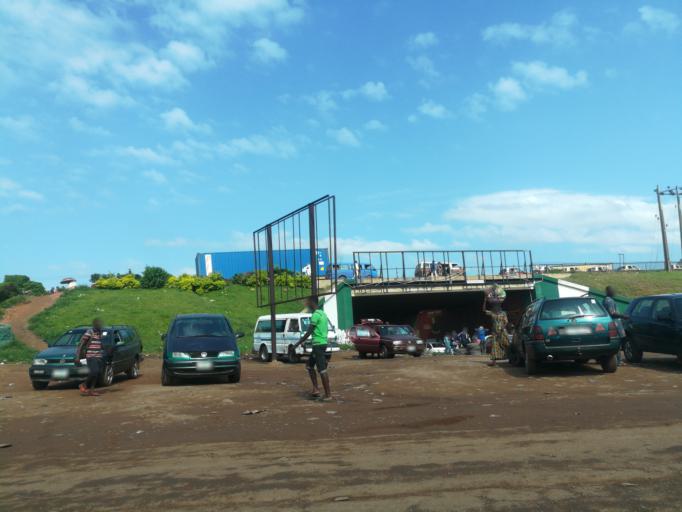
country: NG
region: Oyo
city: Ibadan
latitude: 7.4027
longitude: 3.9433
